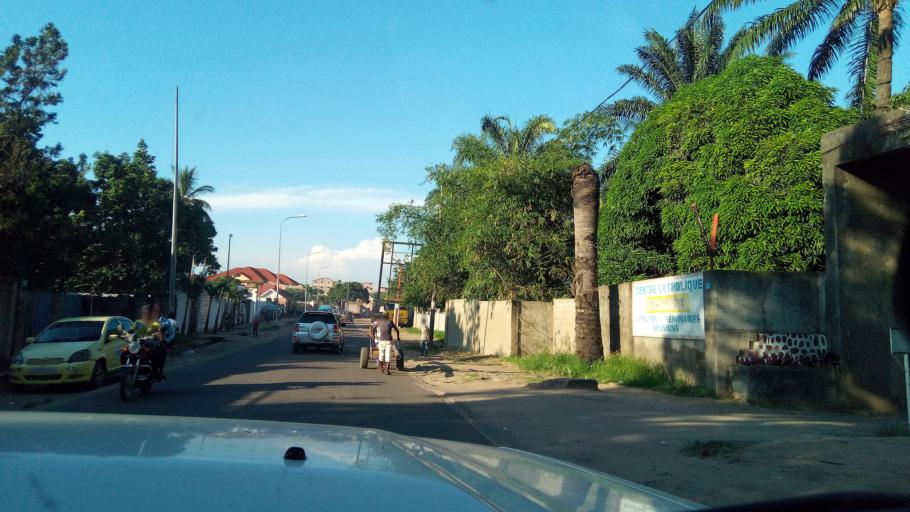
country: CD
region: Kinshasa
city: Kinshasa
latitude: -4.3541
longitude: 15.2635
